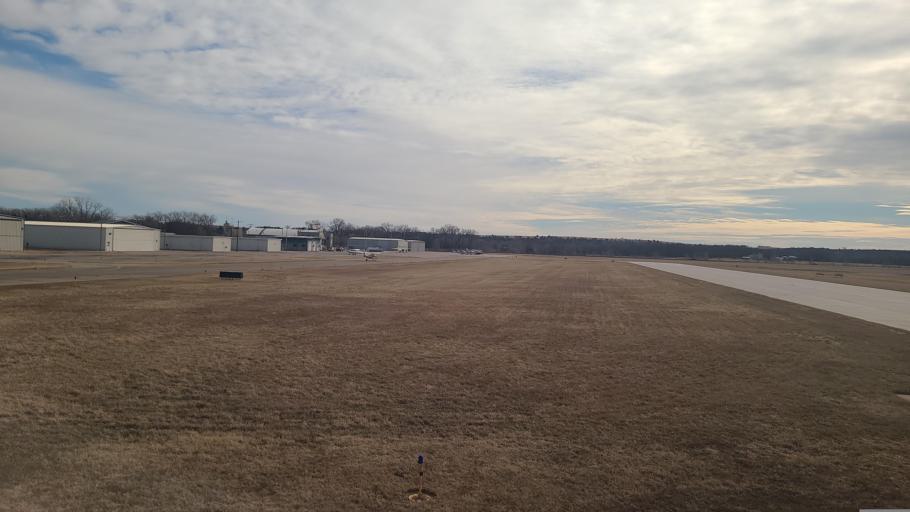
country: US
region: Kansas
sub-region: Riley County
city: Ogden
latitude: 39.1409
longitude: -96.6683
